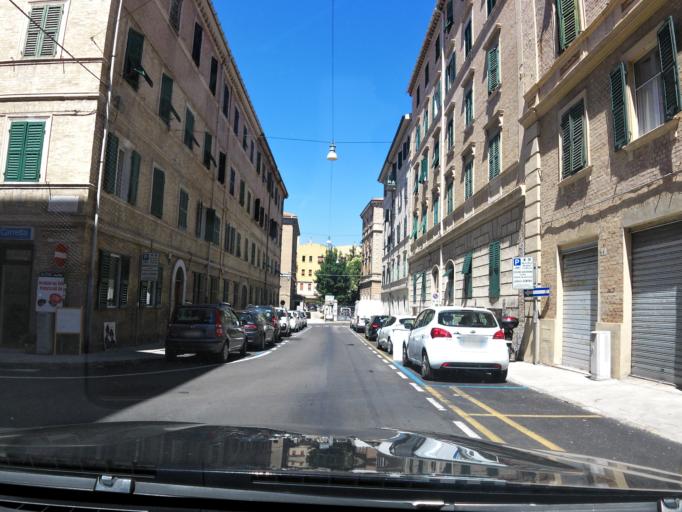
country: IT
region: The Marches
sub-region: Provincia di Ancona
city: Le Grazie di Ancona
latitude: 43.6186
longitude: 13.5177
